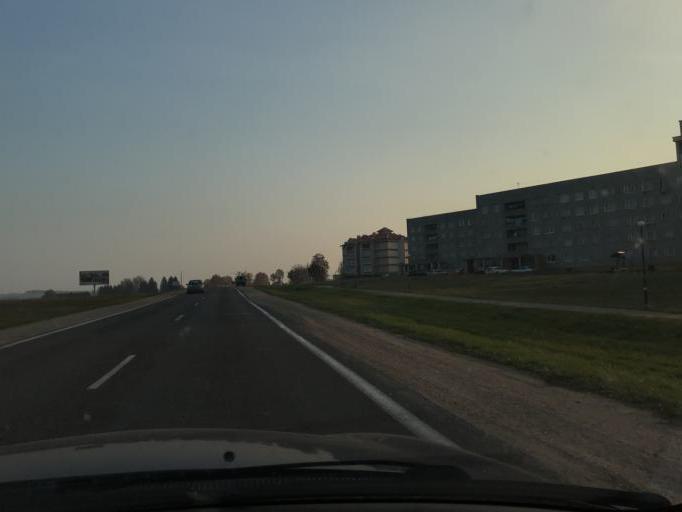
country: BY
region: Grodnenskaya
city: Karelichy
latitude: 53.5619
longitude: 26.1506
